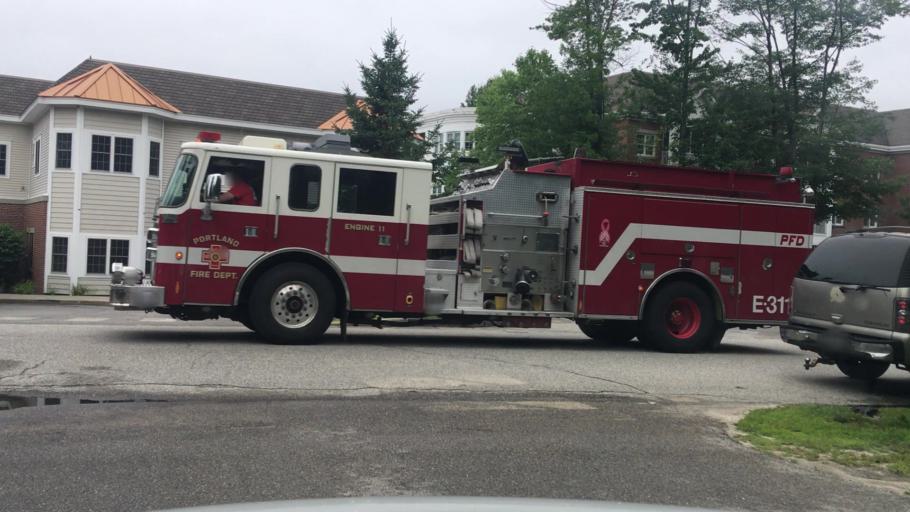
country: US
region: Maine
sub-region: Cumberland County
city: Portland
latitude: 43.6891
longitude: -70.2673
